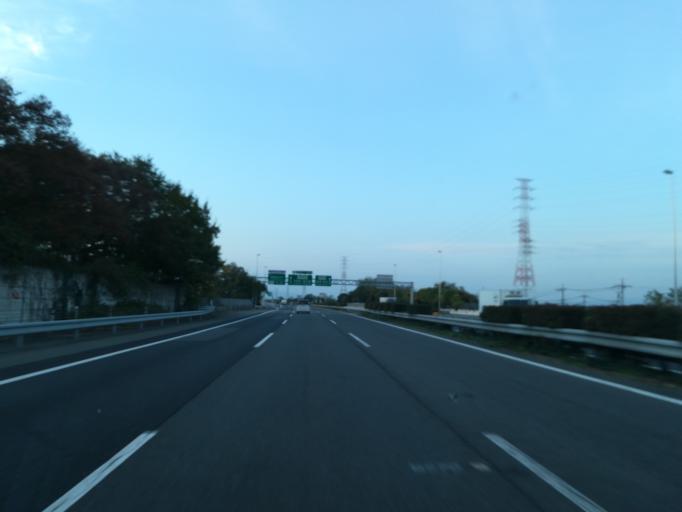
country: JP
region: Gunma
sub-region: Sawa-gun
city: Tamamura
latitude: 36.3079
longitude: 139.0908
